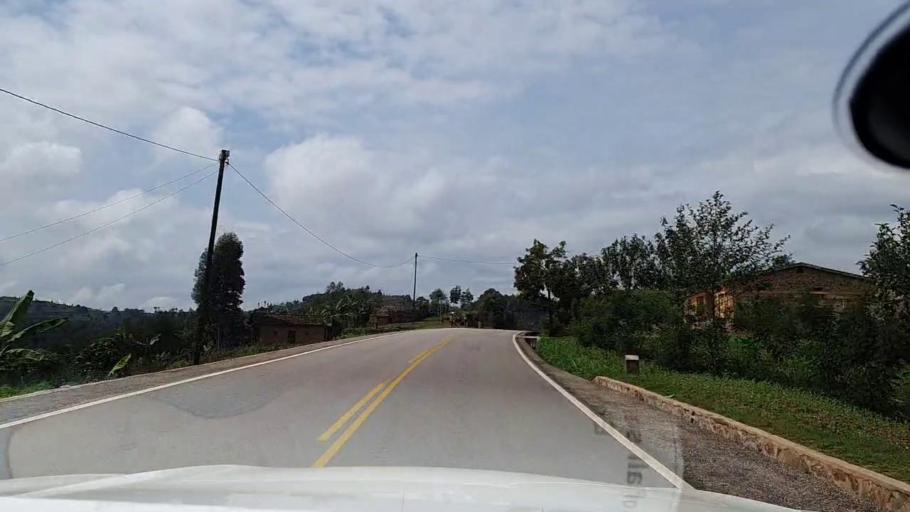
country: RW
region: Southern Province
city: Nzega
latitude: -2.4872
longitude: 29.5133
